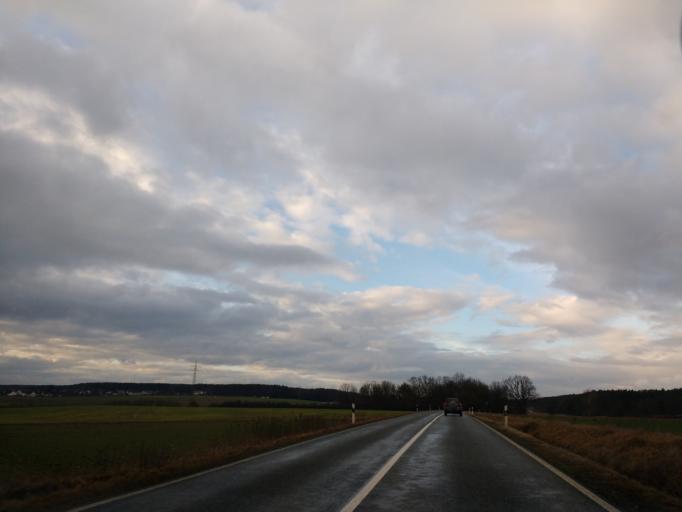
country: DE
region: Bavaria
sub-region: Regierungsbezirk Mittelfranken
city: Weisendorf
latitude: 49.5986
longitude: 10.8434
